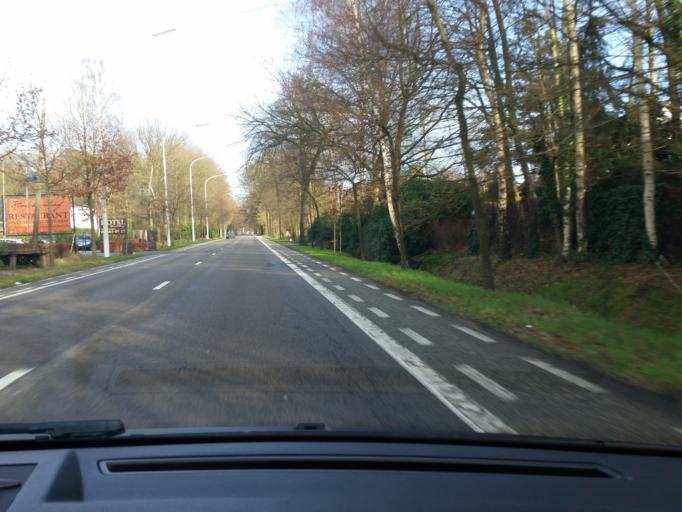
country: BE
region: Flanders
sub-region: Provincie Antwerpen
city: Brasschaat
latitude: 51.3395
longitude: 4.5298
